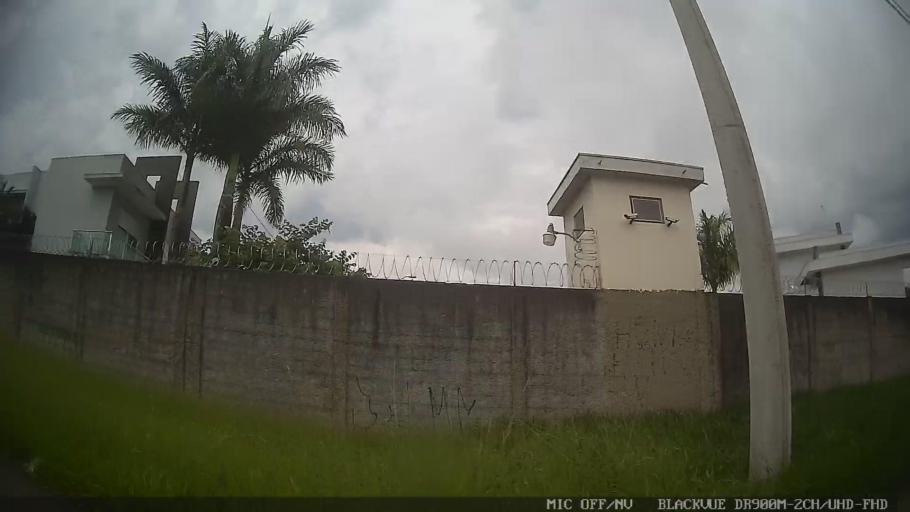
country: BR
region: Sao Paulo
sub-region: Suzano
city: Suzano
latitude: -23.5513
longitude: -46.2998
